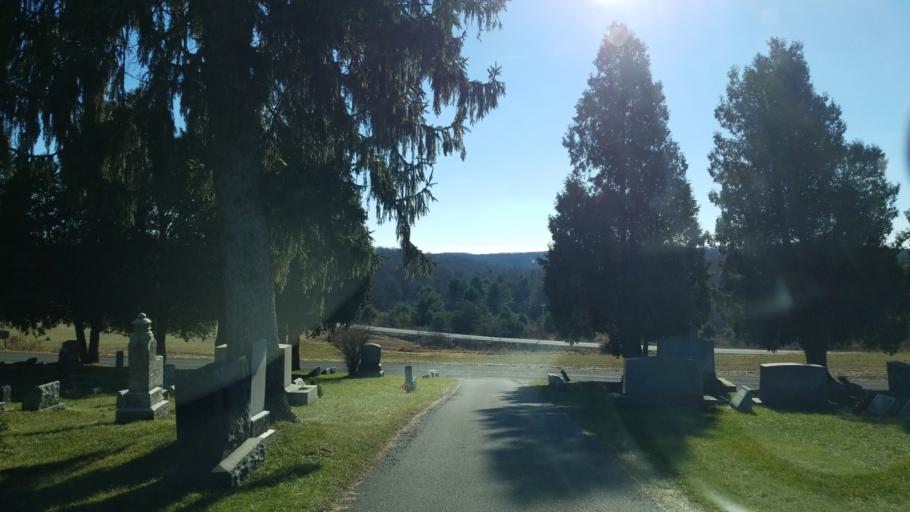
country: US
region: Pennsylvania
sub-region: Jefferson County
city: Falls Creek
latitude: 41.1807
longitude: -78.8640
